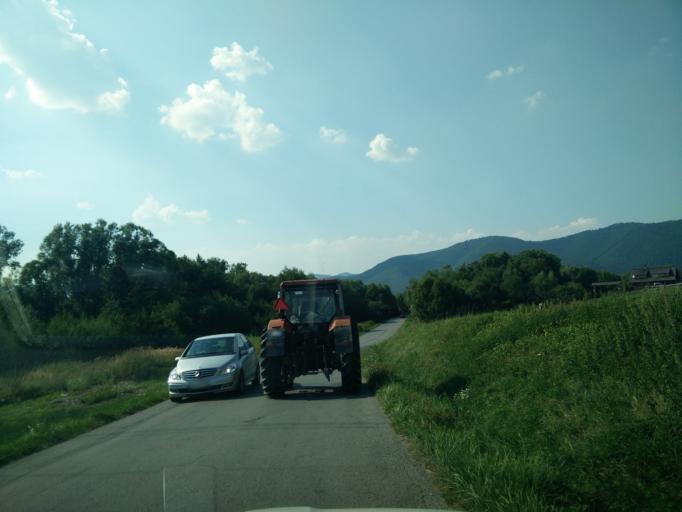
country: SK
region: Zilinsky
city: Rajec
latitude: 49.1083
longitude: 18.6941
